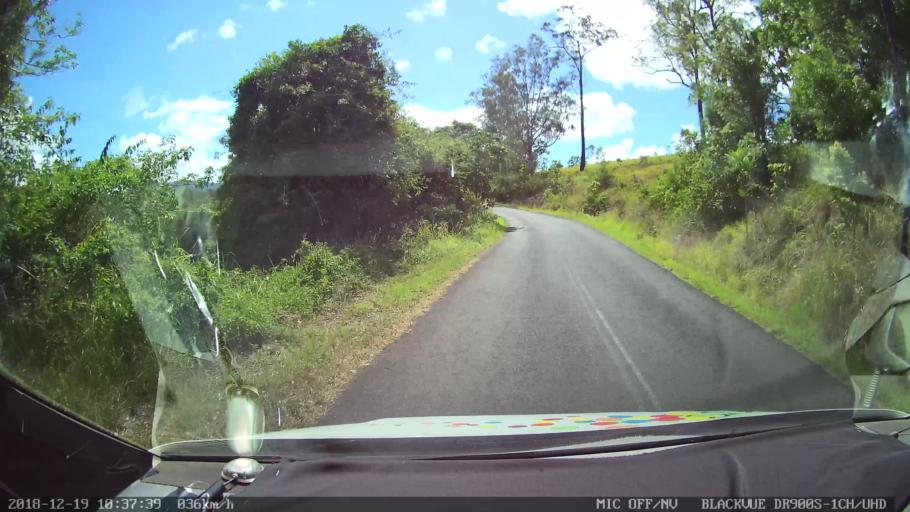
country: AU
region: New South Wales
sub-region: Lismore Municipality
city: Nimbin
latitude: -28.5717
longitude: 153.1530
